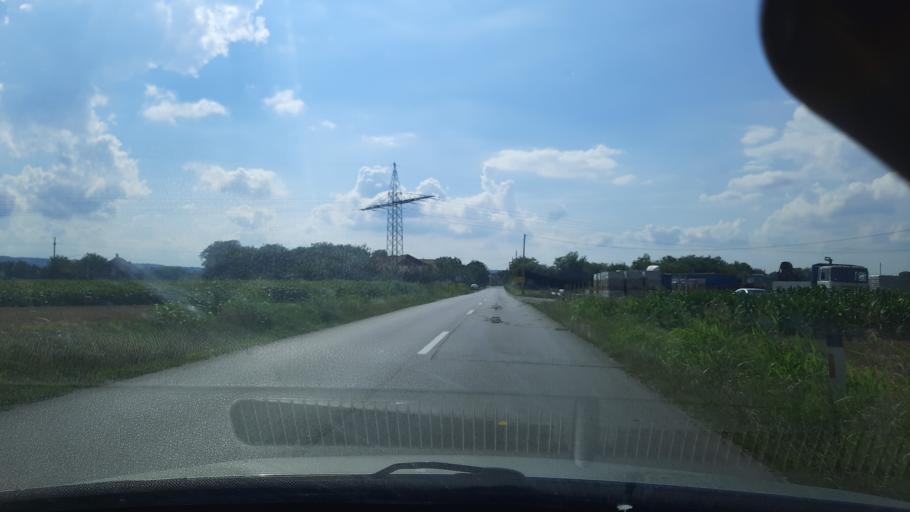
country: RS
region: Central Serbia
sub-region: Branicevski Okrug
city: Malo Crnice
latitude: 44.5868
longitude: 21.2819
